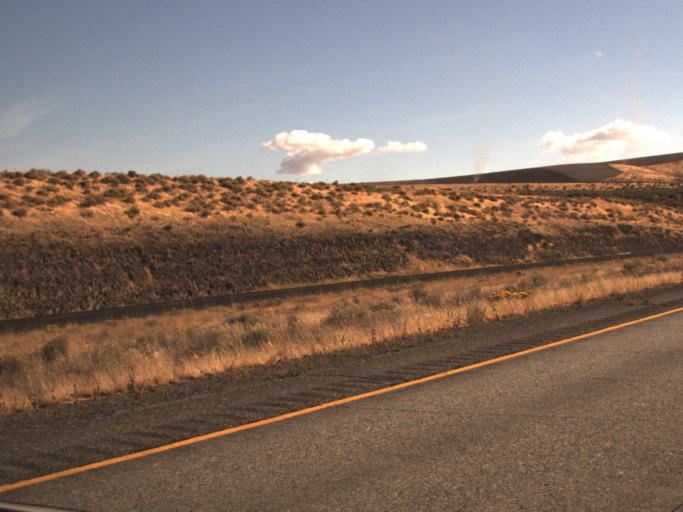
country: US
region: Washington
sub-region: Benton County
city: Highland
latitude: 46.1244
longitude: -119.2025
